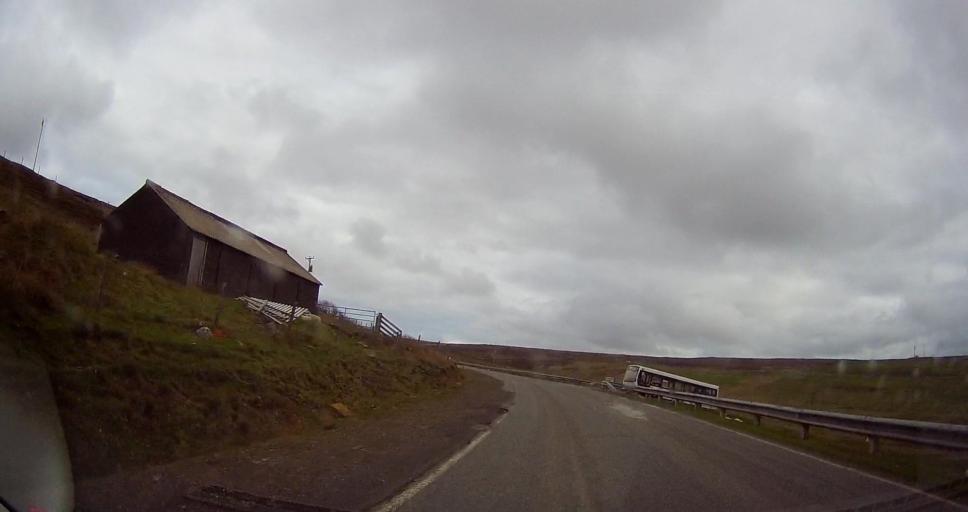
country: GB
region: Scotland
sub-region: Shetland Islands
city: Shetland
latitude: 60.6109
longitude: -1.0740
